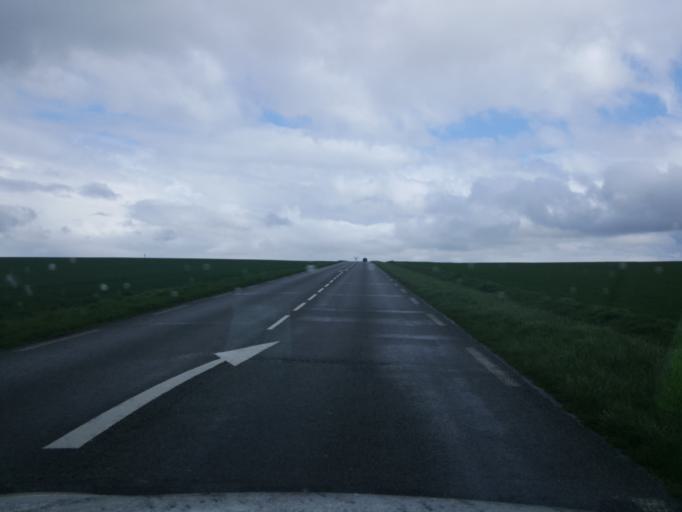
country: FR
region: Picardie
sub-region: Departement de l'Oise
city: Chaumont-en-Vexin
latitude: 49.3061
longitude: 1.8701
